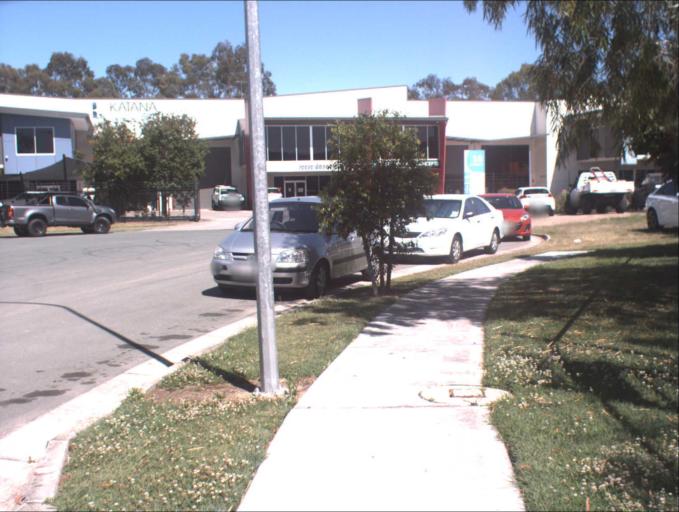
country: AU
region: Queensland
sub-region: Logan
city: Woodridge
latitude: -27.6524
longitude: 153.0750
